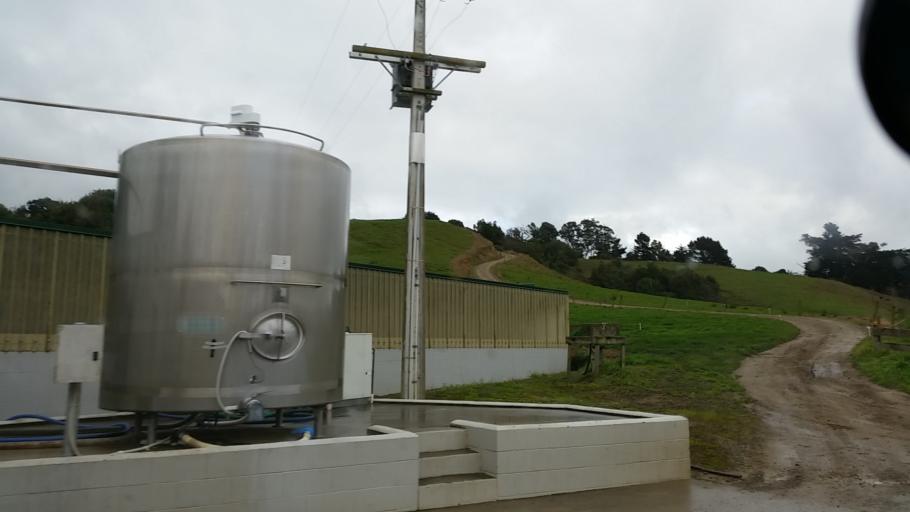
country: NZ
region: Taranaki
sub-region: South Taranaki District
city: Patea
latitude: -39.7574
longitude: 174.7118
